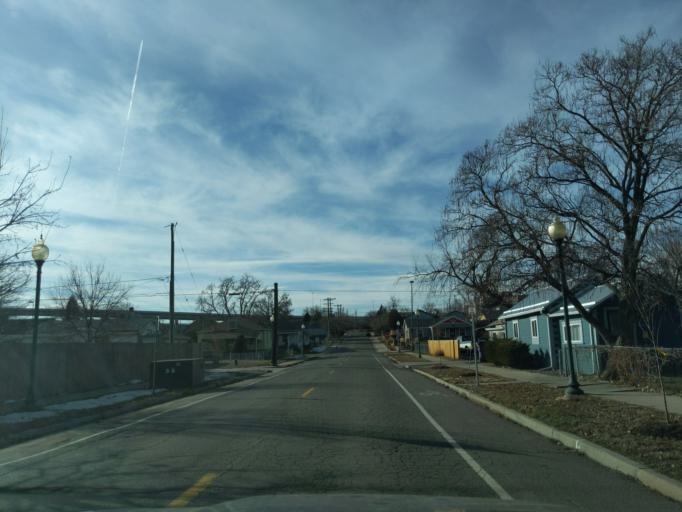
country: US
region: Colorado
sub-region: Denver County
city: Denver
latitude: 39.7819
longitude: -104.9847
